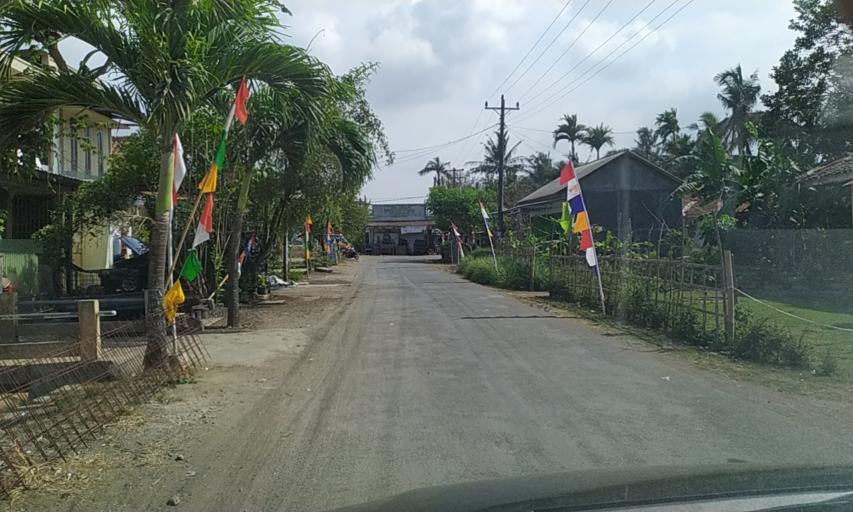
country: ID
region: Central Java
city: Rejanegara
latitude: -7.6619
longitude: 109.0699
